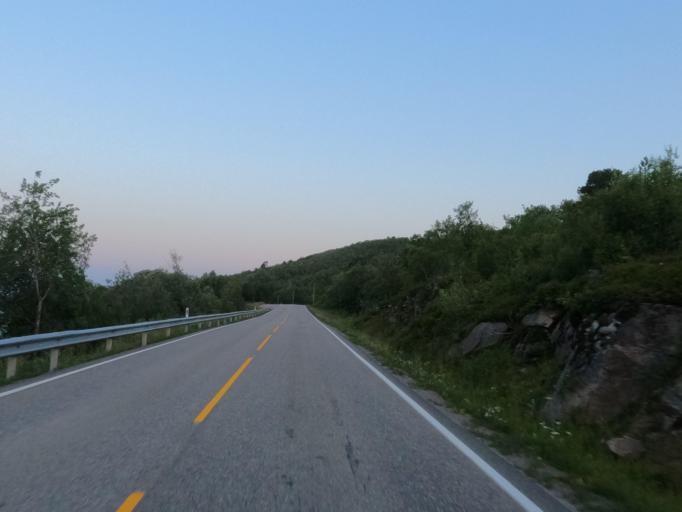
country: NO
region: Nordland
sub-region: Lodingen
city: Lodingen
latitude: 68.5035
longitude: 16.0957
